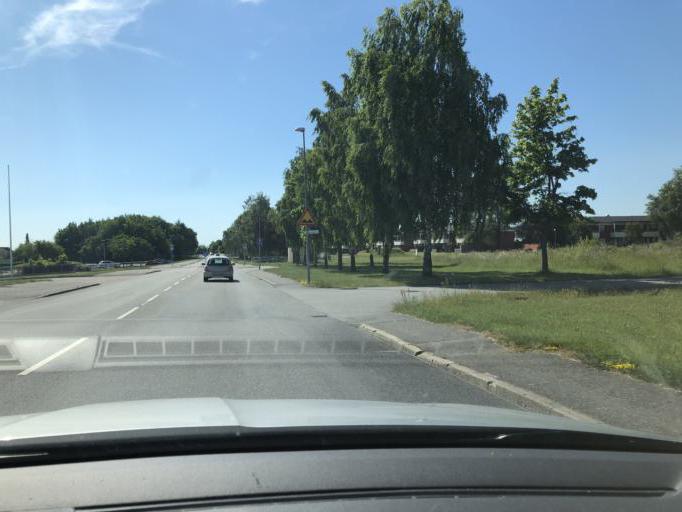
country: SE
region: Skane
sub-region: Bromolla Kommun
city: Bromoella
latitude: 56.0761
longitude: 14.4915
